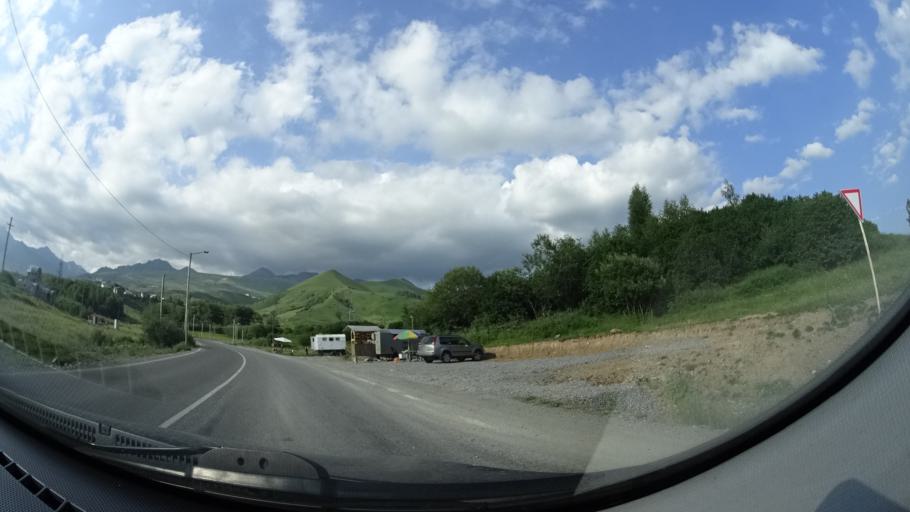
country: GE
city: Gudauri
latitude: 42.4476
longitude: 44.4882
